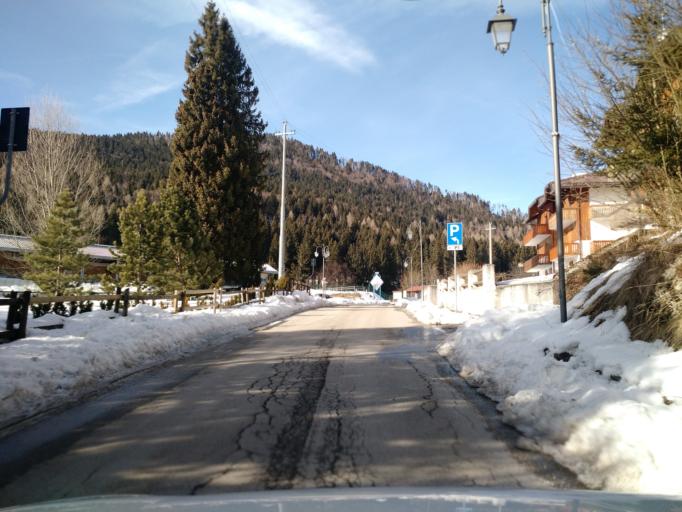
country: IT
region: Veneto
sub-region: Provincia di Vicenza
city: Roana
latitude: 45.8871
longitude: 11.4606
